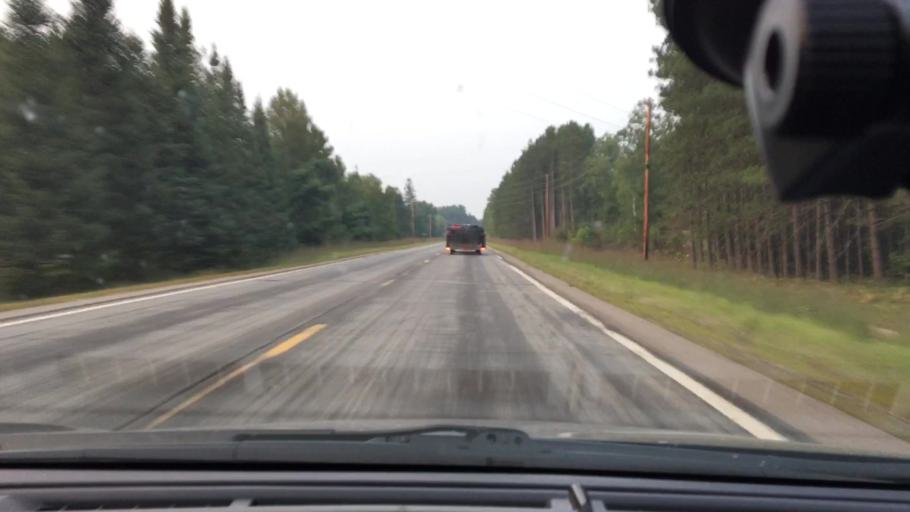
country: US
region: Minnesota
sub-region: Crow Wing County
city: Cross Lake
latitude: 46.7983
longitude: -93.9609
